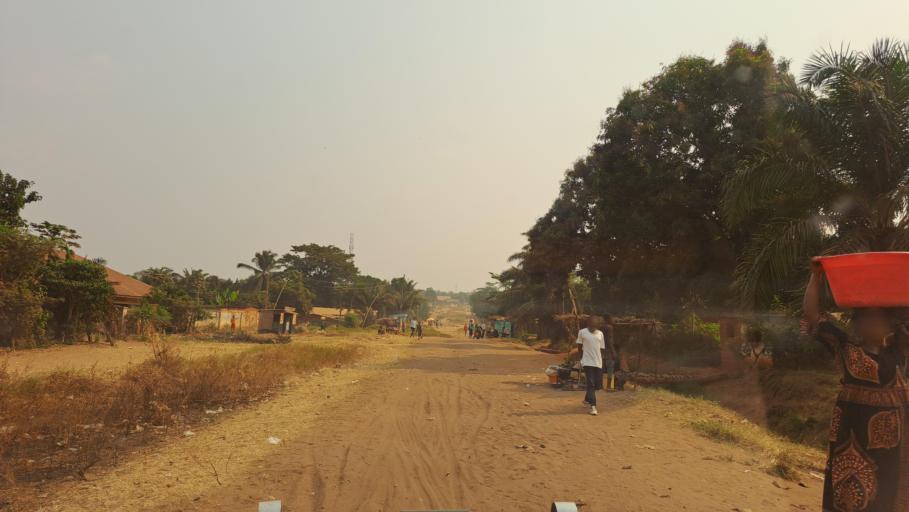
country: CD
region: Kasai-Oriental
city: Mbuji-Mayi
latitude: -6.1236
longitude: 23.6043
